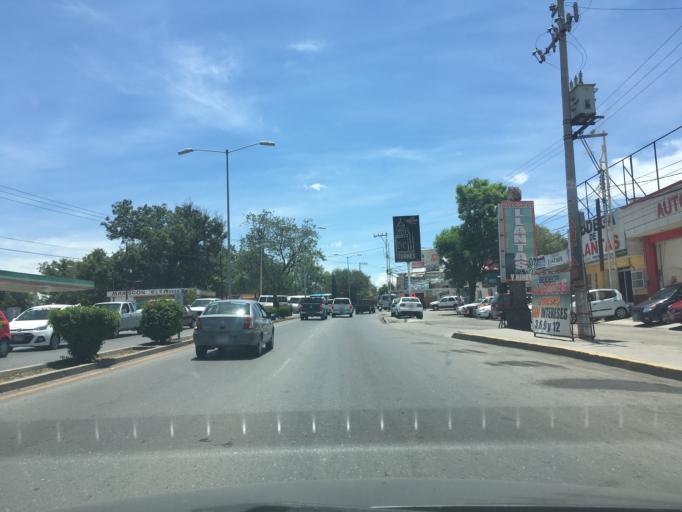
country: MX
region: Hidalgo
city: Ixmiquilpan
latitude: 20.4801
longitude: -99.2279
